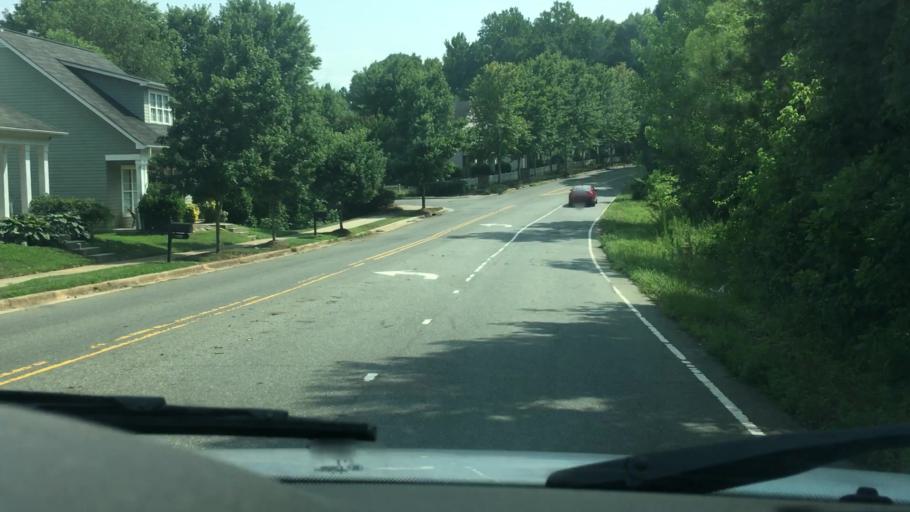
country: US
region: North Carolina
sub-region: Mecklenburg County
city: Huntersville
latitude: 35.4063
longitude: -80.9059
